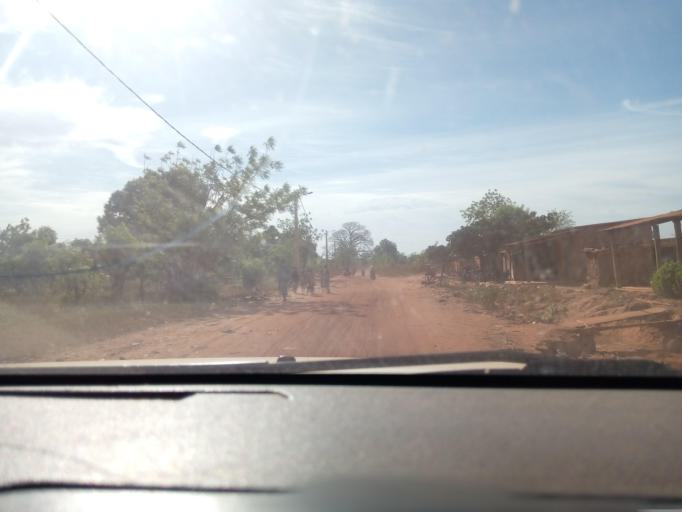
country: ML
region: Sikasso
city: Sikasso
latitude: 11.8467
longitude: -6.0141
